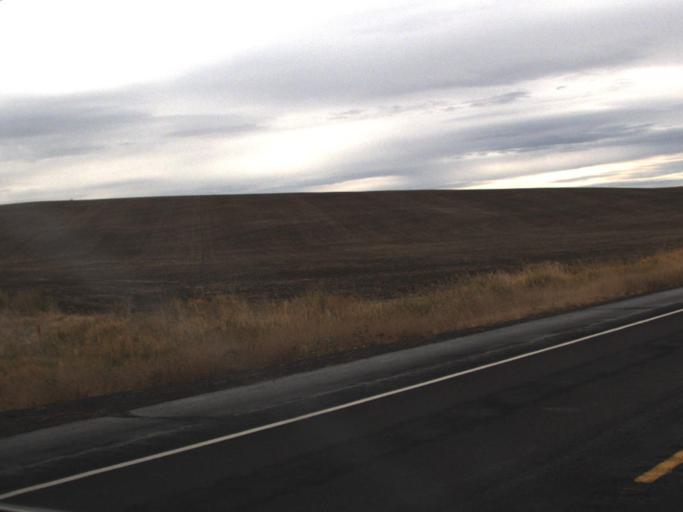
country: US
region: Washington
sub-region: Asotin County
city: Clarkston
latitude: 46.5159
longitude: -117.0810
